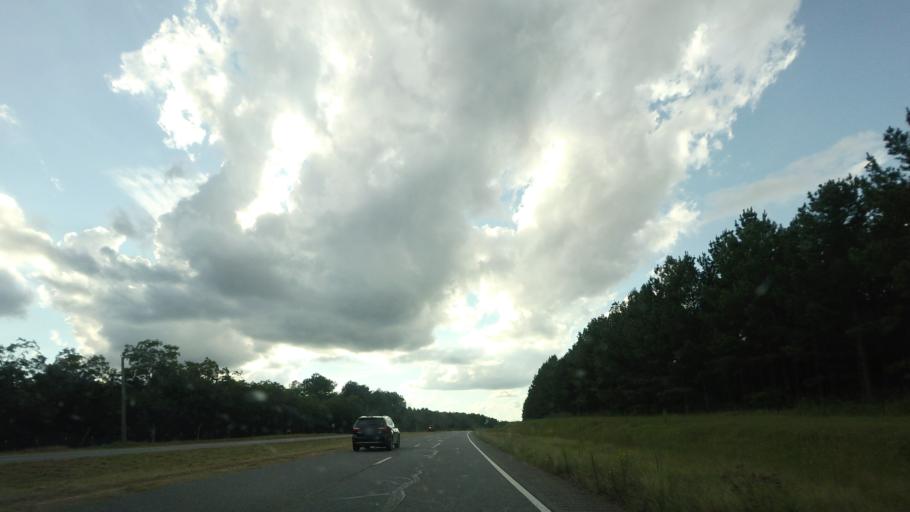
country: US
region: Georgia
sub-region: Houston County
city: Perry
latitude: 32.4132
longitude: -83.6765
